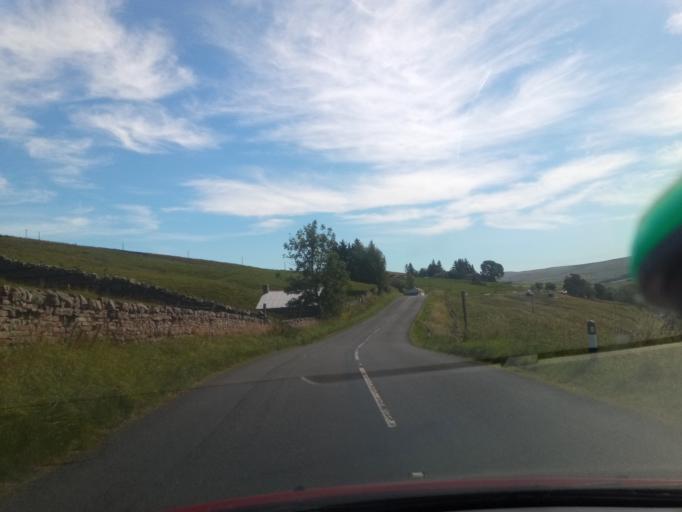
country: GB
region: England
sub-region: County Durham
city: Holwick
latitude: 54.7664
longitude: -2.2362
